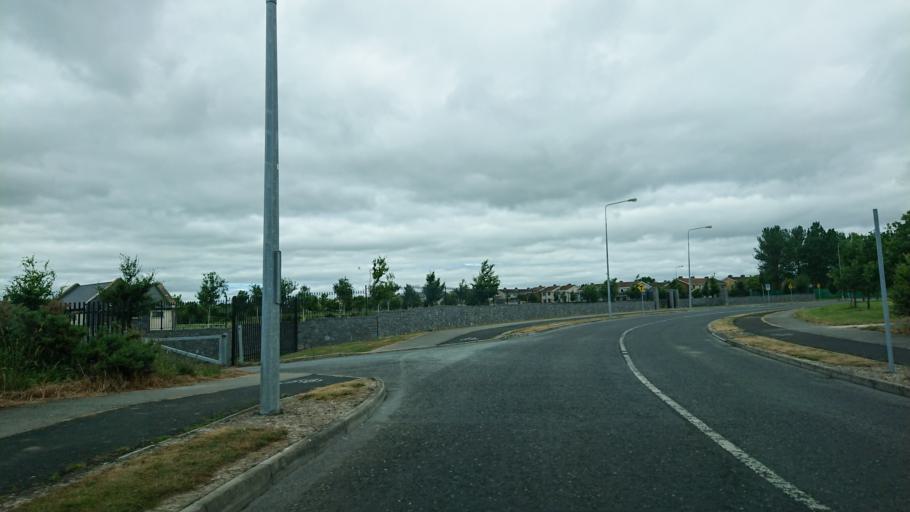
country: IE
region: Munster
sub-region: Waterford
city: Waterford
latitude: 52.2383
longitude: -7.1448
